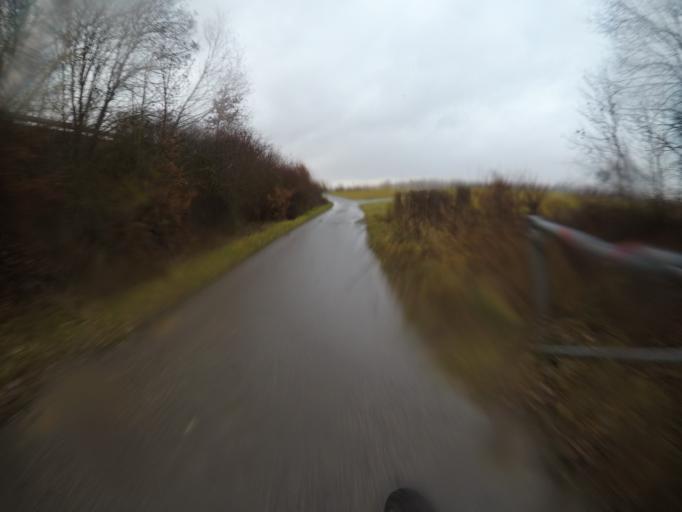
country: DE
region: Baden-Wuerttemberg
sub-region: Regierungsbezirk Stuttgart
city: Boeblingen
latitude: 48.6720
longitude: 8.9821
